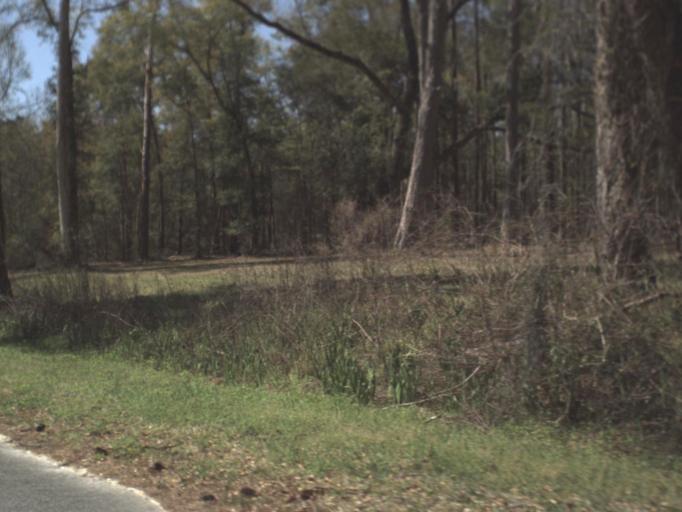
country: US
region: Florida
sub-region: Jefferson County
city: Monticello
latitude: 30.5005
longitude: -84.0245
